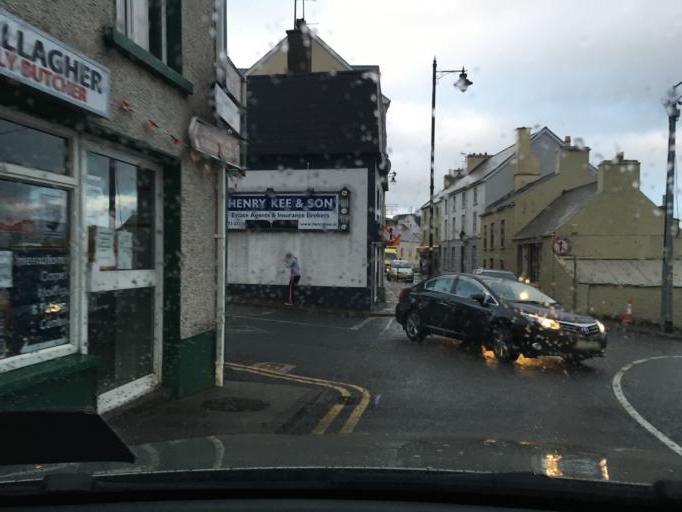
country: IE
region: Ulster
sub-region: County Donegal
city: Killybegs
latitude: 54.6365
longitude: -8.4453
